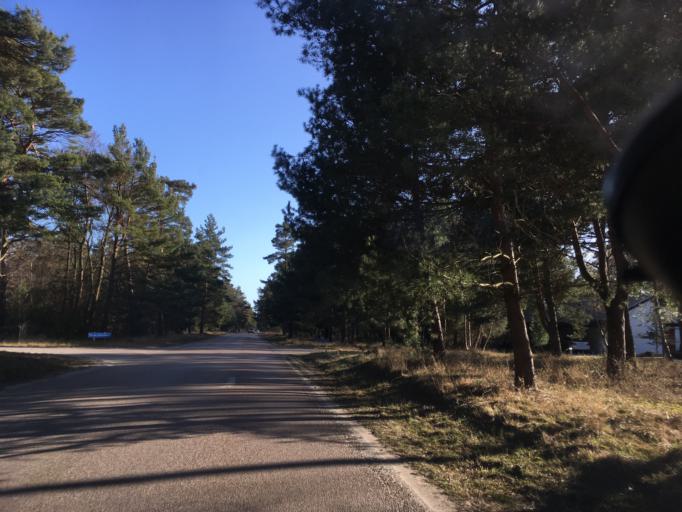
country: SE
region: Skane
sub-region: Vellinge Kommun
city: Ljunghusen
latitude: 55.4017
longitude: 12.9212
